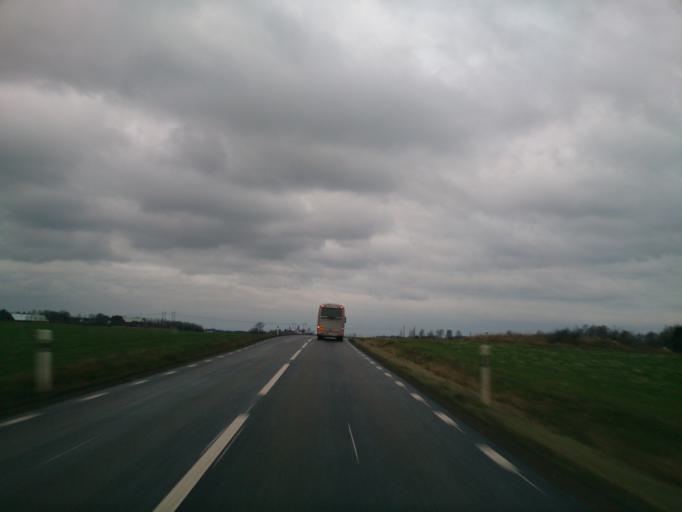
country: SE
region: OEstergoetland
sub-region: Linkopings Kommun
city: Linghem
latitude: 58.3898
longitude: 15.7787
